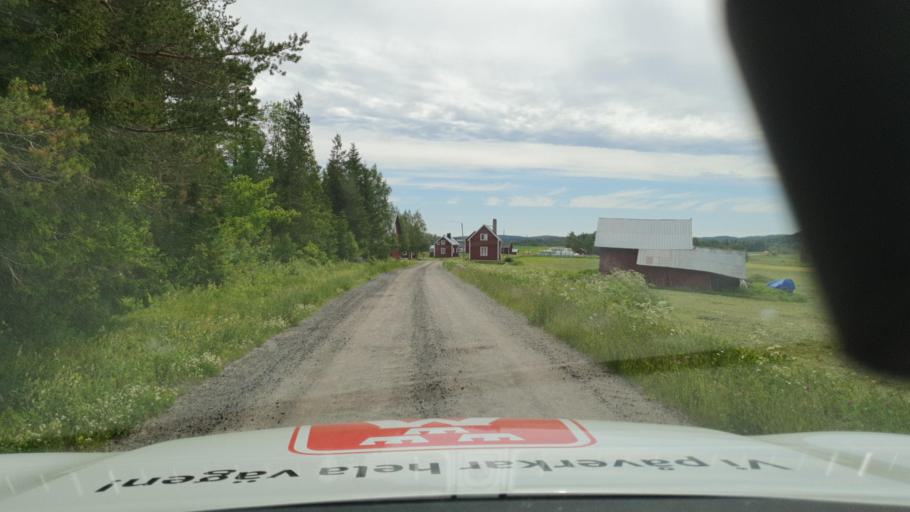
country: SE
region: Vaesterbotten
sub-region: Robertsfors Kommun
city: Robertsfors
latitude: 64.2755
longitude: 20.6218
